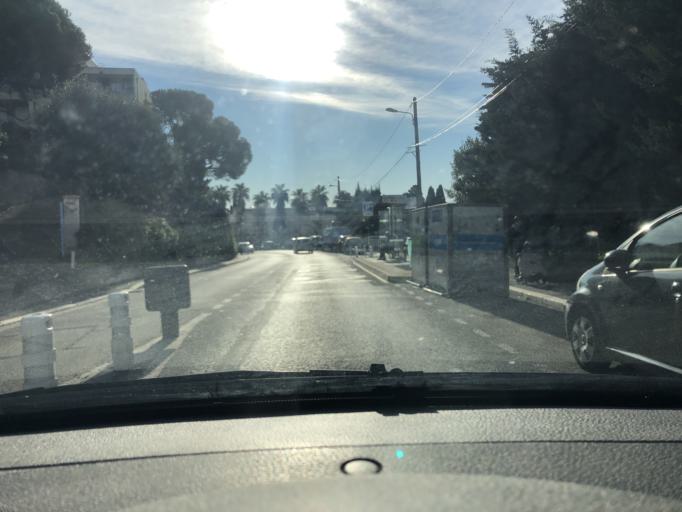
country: FR
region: Provence-Alpes-Cote d'Azur
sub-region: Departement des Alpes-Maritimes
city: Saint-Laurent-du-Var
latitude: 43.6784
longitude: 7.2134
